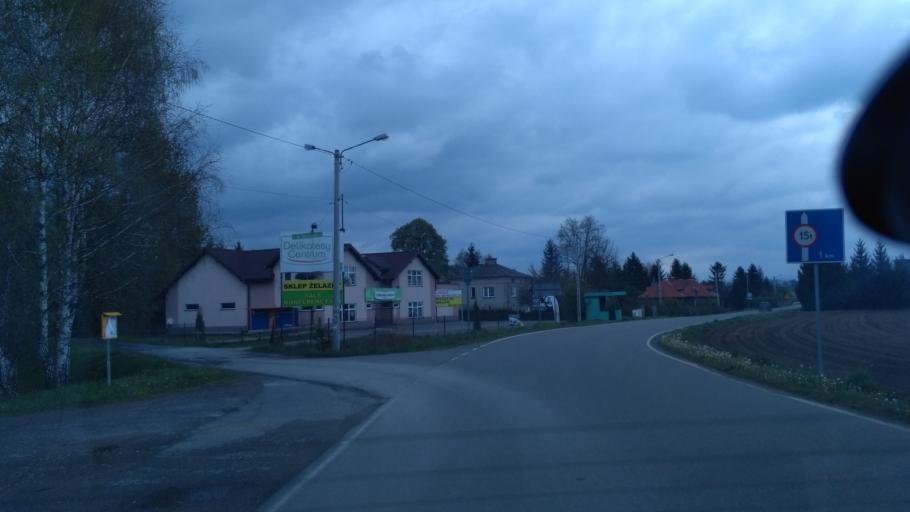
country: PL
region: Subcarpathian Voivodeship
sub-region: Powiat brzozowski
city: Turze Pole
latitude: 49.6585
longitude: 21.9962
